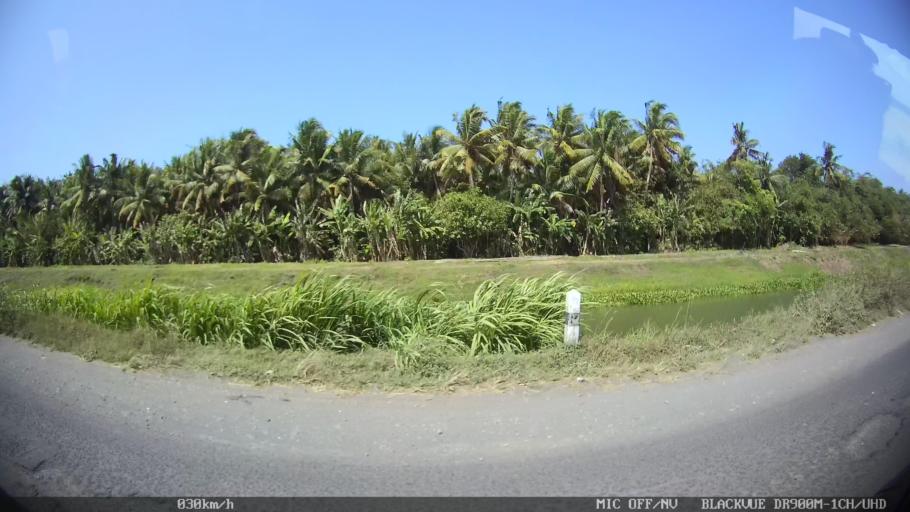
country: ID
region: Daerah Istimewa Yogyakarta
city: Srandakan
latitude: -7.9484
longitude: 110.1825
